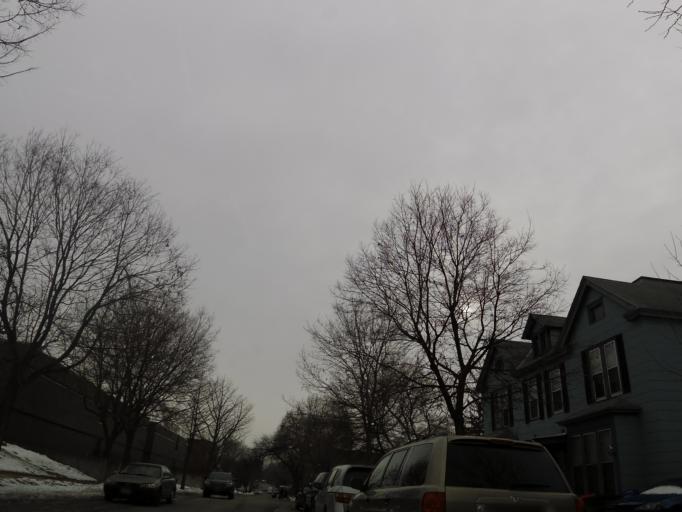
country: US
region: Minnesota
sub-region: Ramsey County
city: Saint Paul
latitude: 44.9548
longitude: -93.0678
